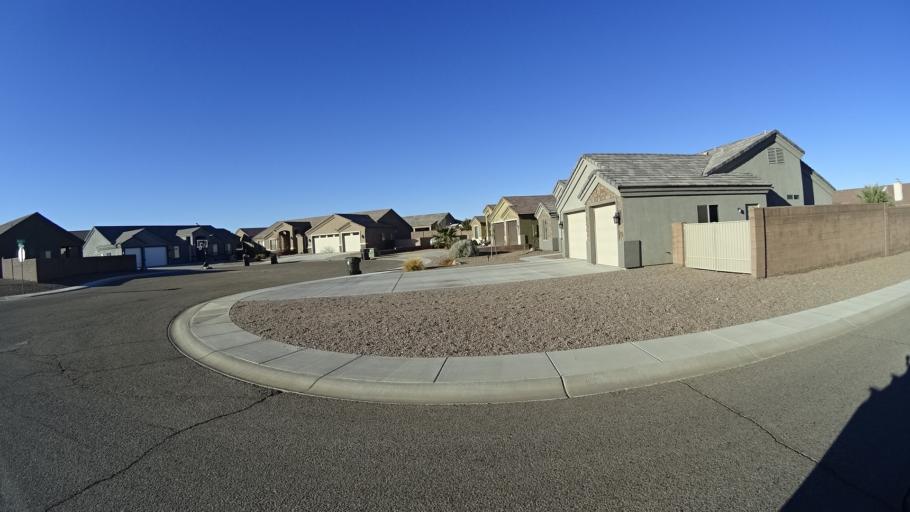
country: US
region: Arizona
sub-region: Mohave County
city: New Kingman-Butler
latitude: 35.2206
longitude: -113.9707
